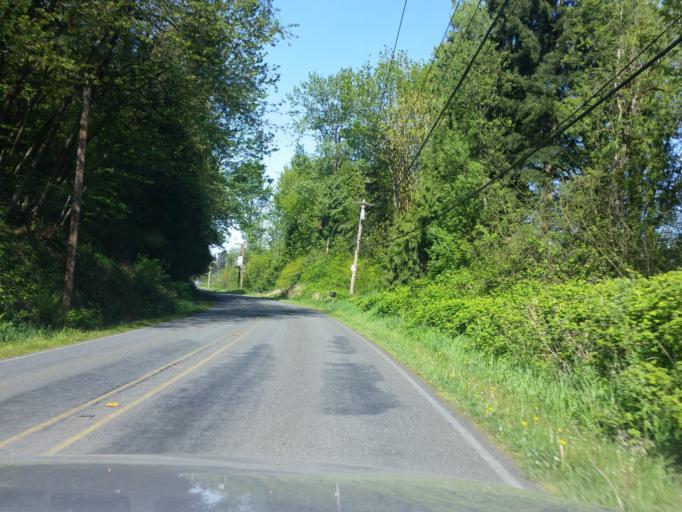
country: US
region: Washington
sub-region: Snohomish County
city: Cathcart
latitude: 47.8769
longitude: -122.1050
